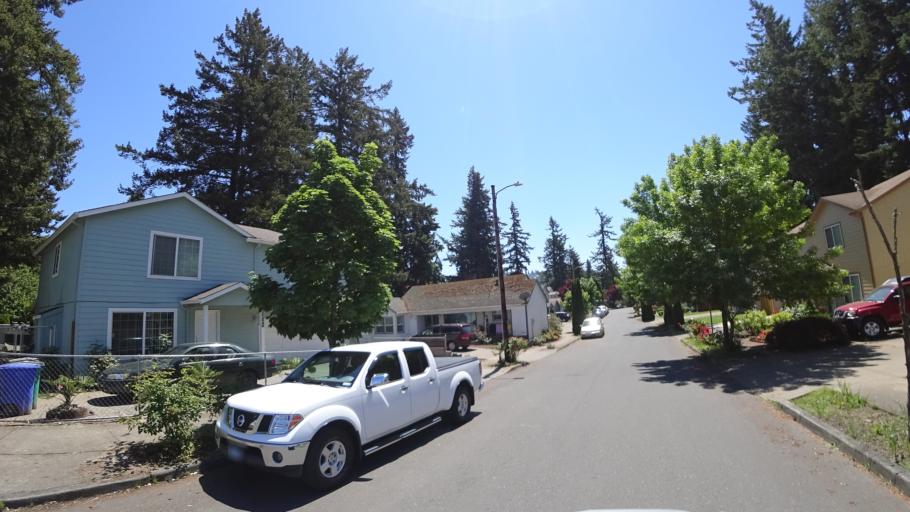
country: US
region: Oregon
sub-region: Clackamas County
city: Happy Valley
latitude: 45.4834
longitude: -122.5263
